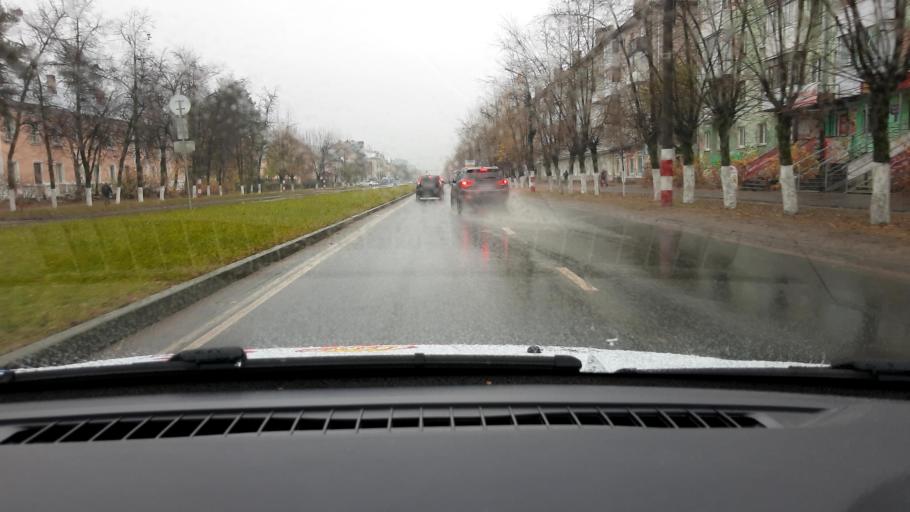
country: RU
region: Nizjnij Novgorod
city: Dzerzhinsk
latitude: 56.2449
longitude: 43.4359
